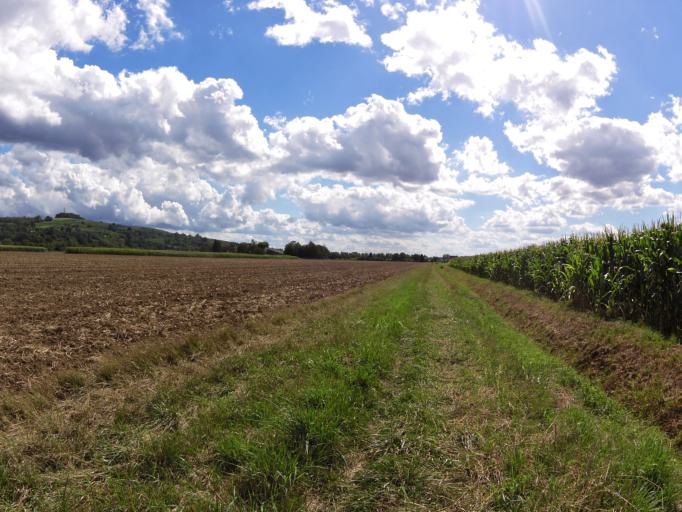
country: DE
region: Baden-Wuerttemberg
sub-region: Freiburg Region
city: Lahr
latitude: 48.3662
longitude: 7.8475
